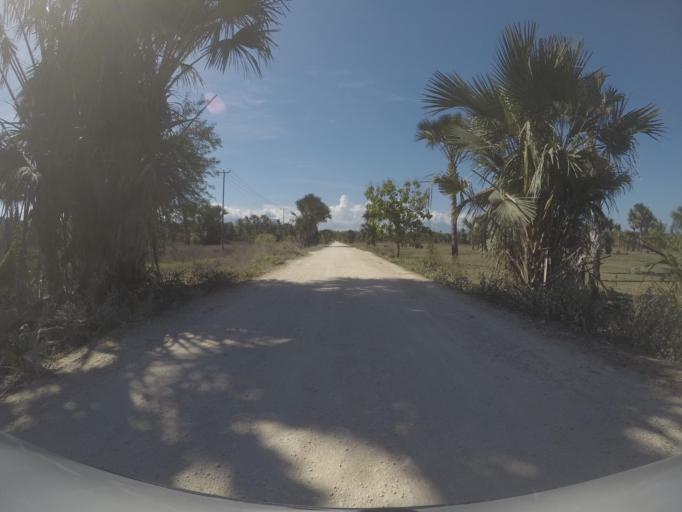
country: TL
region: Viqueque
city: Viqueque
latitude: -8.8909
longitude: 126.5068
